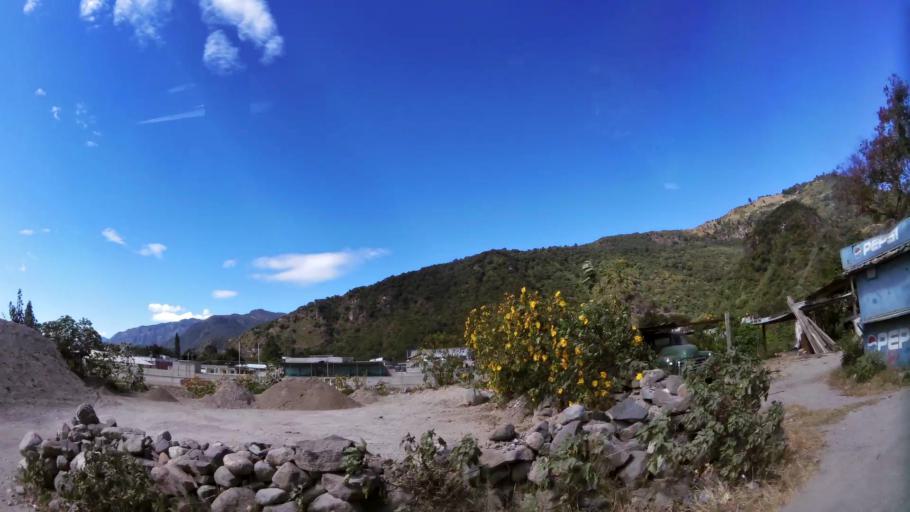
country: GT
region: Solola
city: Panajachel
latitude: 14.7420
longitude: -91.1513
